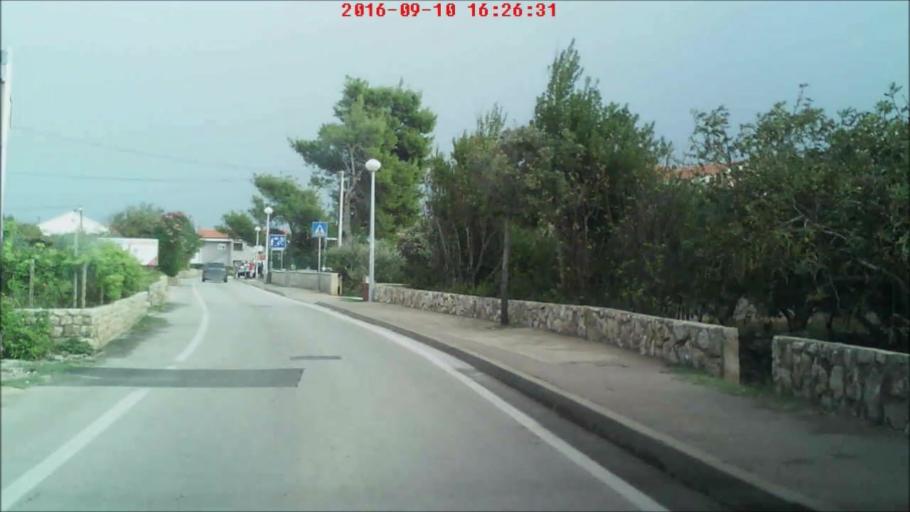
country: HR
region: Zadarska
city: Vir
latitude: 44.3006
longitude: 15.0840
